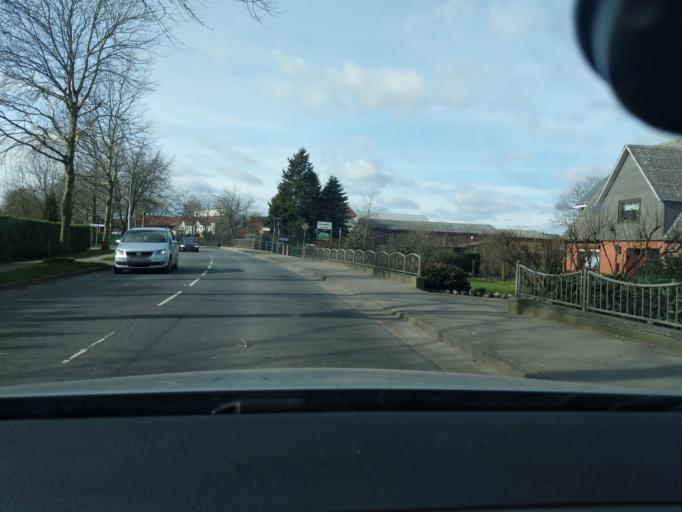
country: DE
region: Lower Saxony
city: Drochtersen
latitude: 53.7074
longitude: 9.3948
